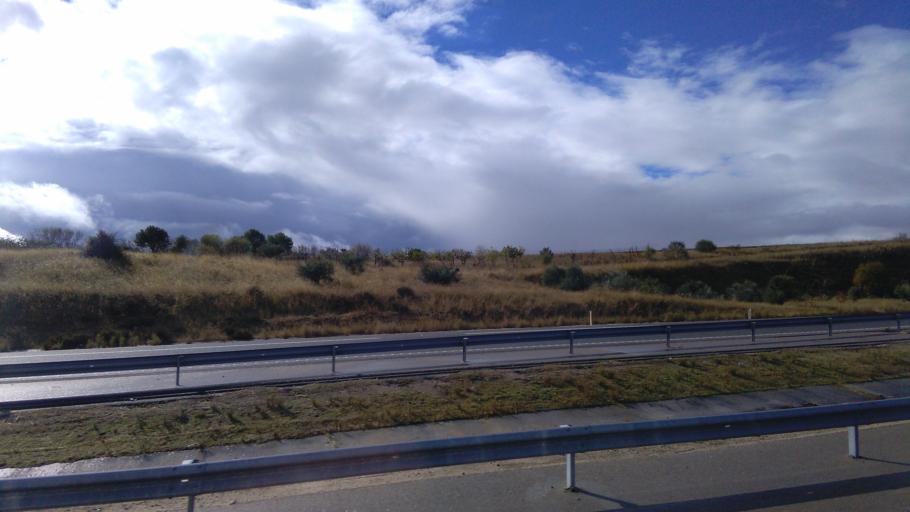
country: ES
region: Madrid
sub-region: Provincia de Madrid
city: Navalcarnero
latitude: 40.2656
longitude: -4.0239
